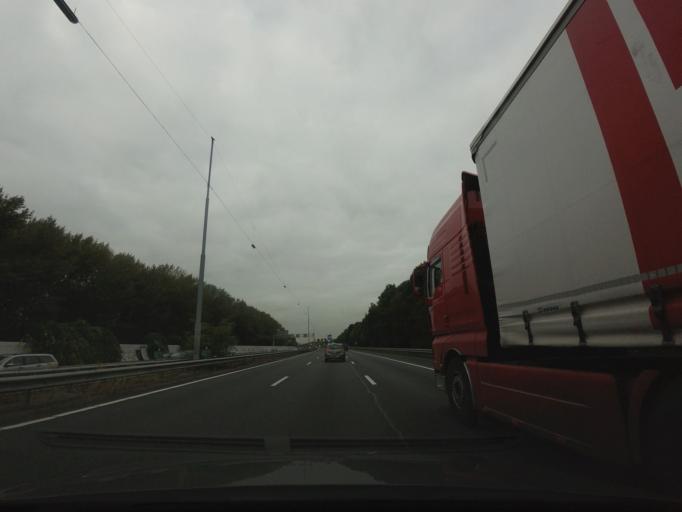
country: NL
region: North Holland
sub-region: Gemeente Waterland
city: Broek in Waterland
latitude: 52.3984
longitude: 4.9591
